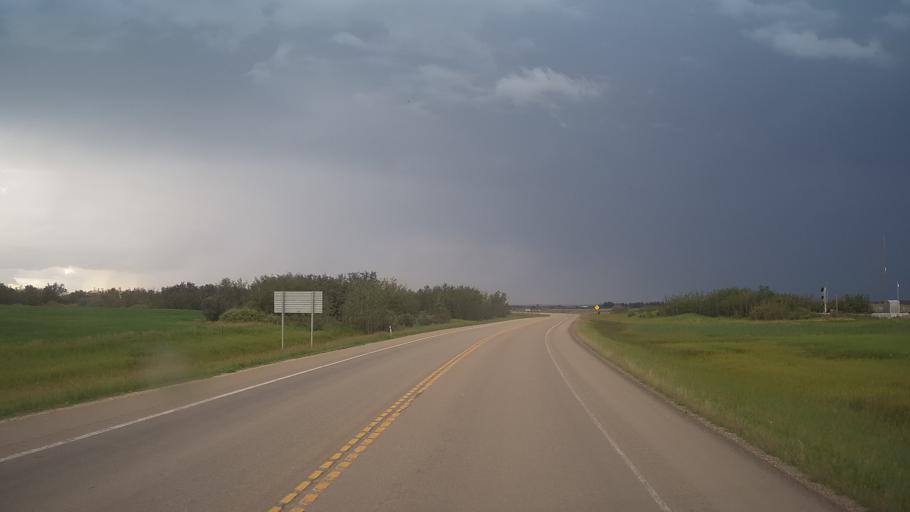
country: CA
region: Alberta
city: Tofield
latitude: 53.2915
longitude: -112.4454
